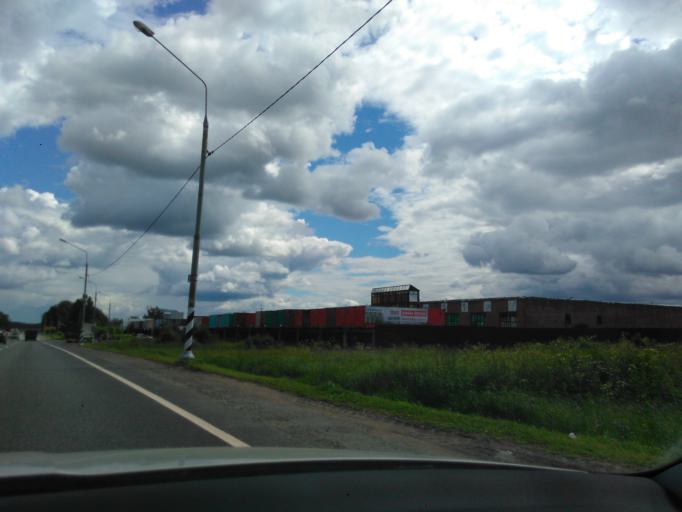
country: RU
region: Moskovskaya
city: Solnechnogorsk
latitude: 56.2381
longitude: 36.8958
